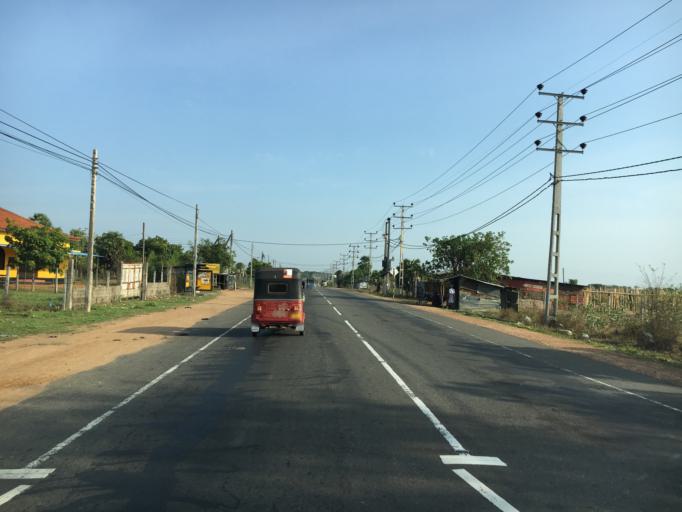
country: LK
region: Eastern Province
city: Eravur Town
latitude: 7.9318
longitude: 81.5116
